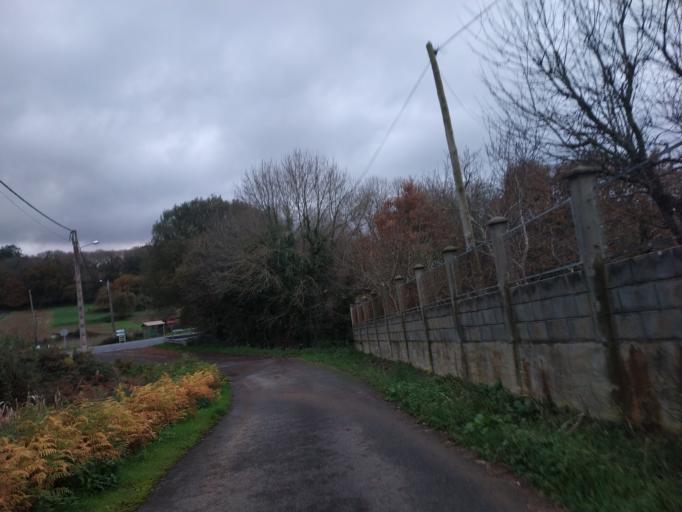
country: ES
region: Galicia
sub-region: Provincia de Pontevedra
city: Silleda
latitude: 42.7814
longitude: -8.1718
